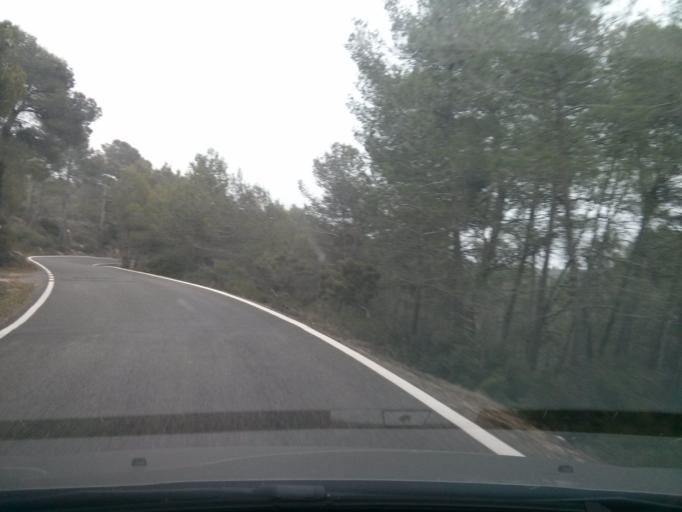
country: ES
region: Catalonia
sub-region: Provincia de Tarragona
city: Sant Jaume dels Domenys
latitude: 41.3361
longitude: 1.5302
